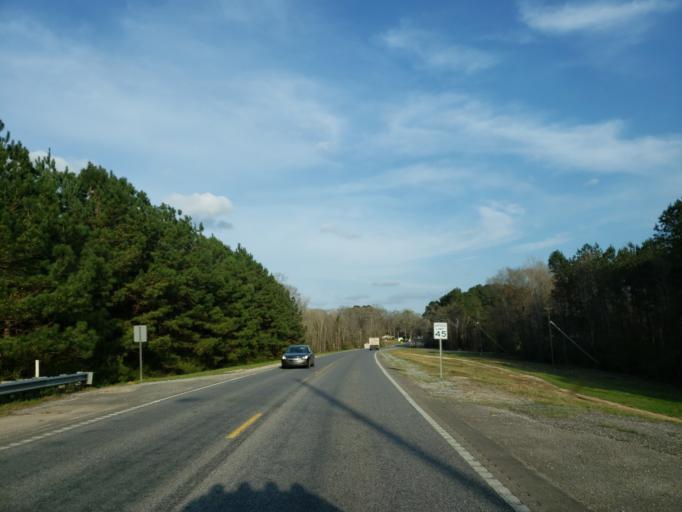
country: US
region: Mississippi
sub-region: Clarke County
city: Stonewall
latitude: 32.1762
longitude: -88.8171
